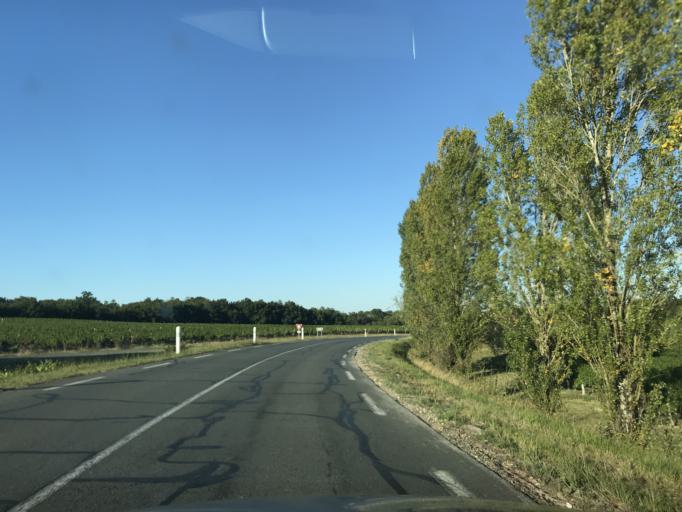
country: FR
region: Aquitaine
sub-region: Departement de la Gironde
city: Castets-en-Dorthe
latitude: 44.6200
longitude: -0.1641
